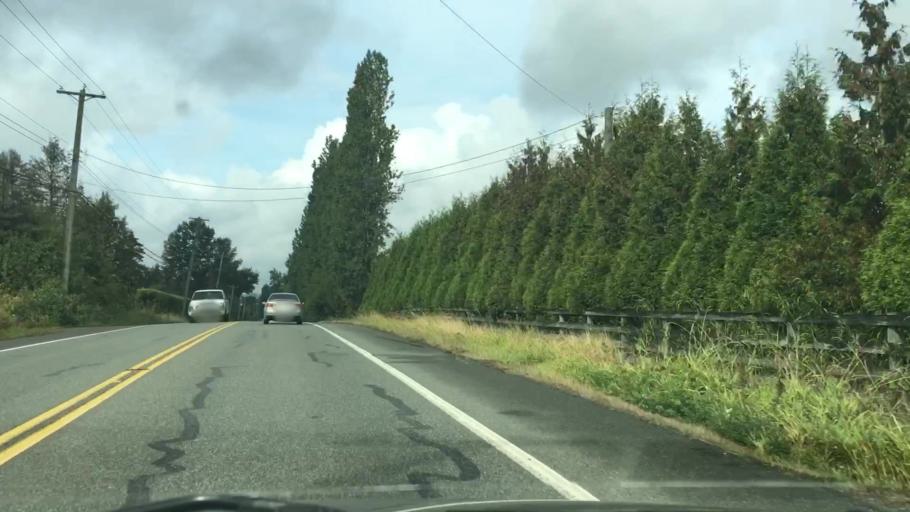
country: CA
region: British Columbia
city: Langley
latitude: 49.1045
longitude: -122.5949
